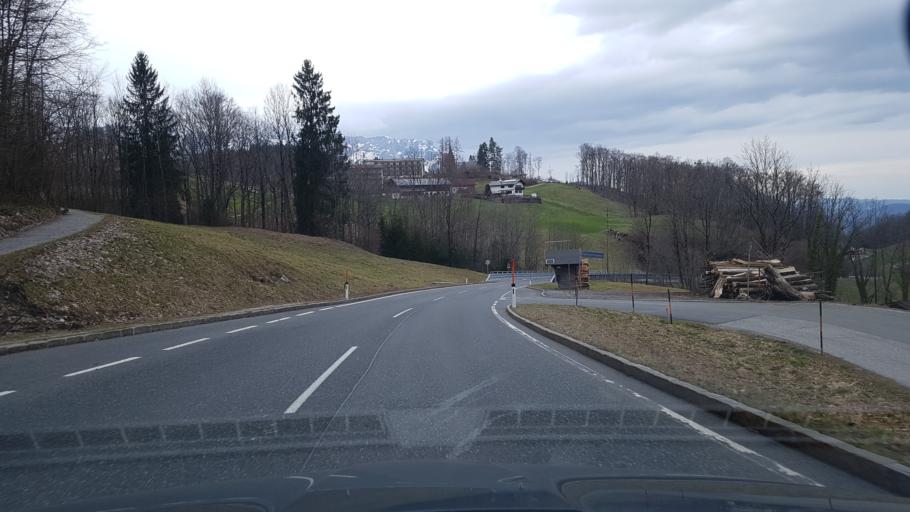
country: AT
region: Salzburg
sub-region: Politischer Bezirk Hallein
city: Hallein
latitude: 47.6619
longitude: 13.0951
